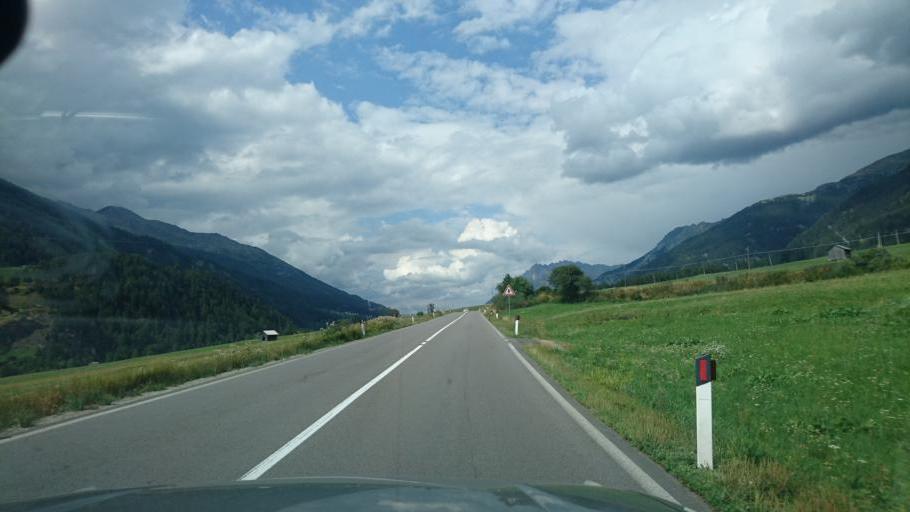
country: IT
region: Trentino-Alto Adige
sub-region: Bolzano
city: Malles Venosta
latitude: 46.7287
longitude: 10.5387
